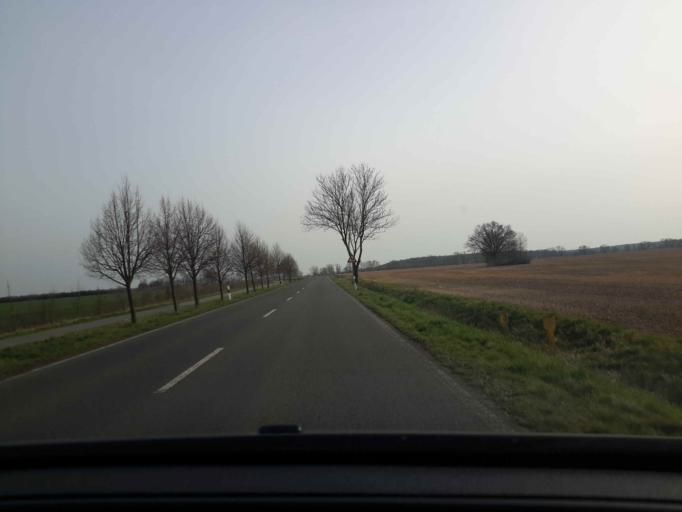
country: DE
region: Saxony
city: Rackwitz
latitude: 51.4316
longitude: 12.3551
